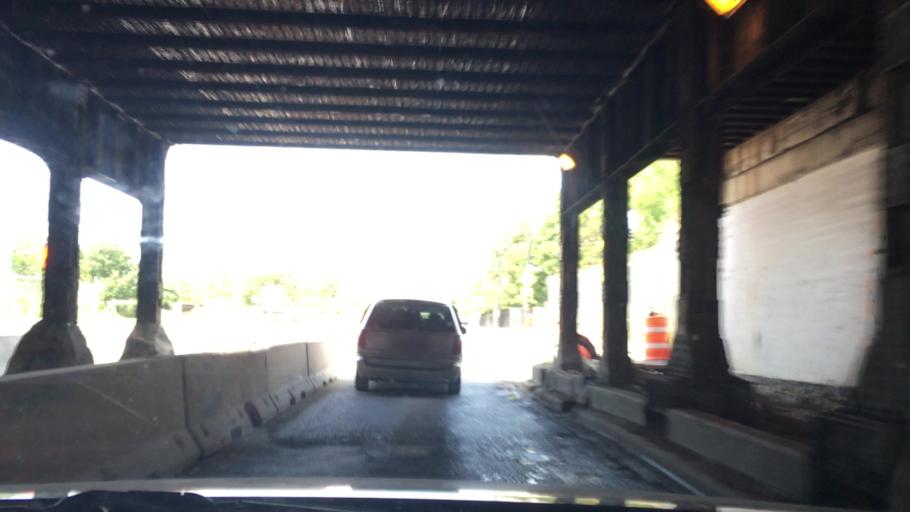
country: US
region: Illinois
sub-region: Cook County
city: Chicago
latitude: 41.8608
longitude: -87.6662
